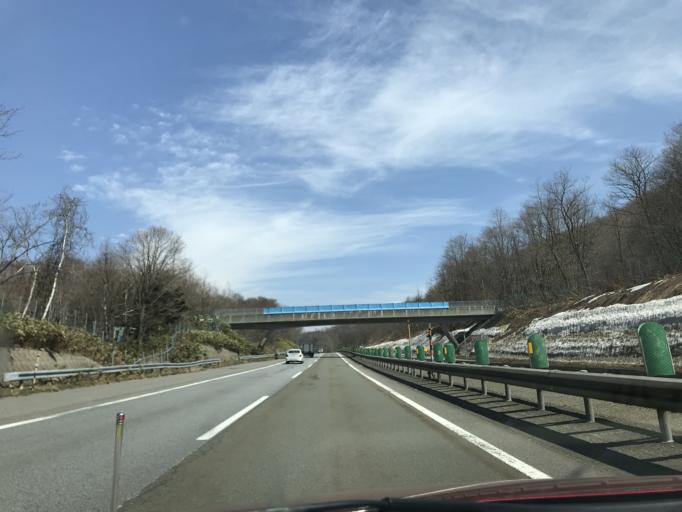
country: JP
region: Hokkaido
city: Bibai
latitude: 43.2828
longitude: 141.8564
